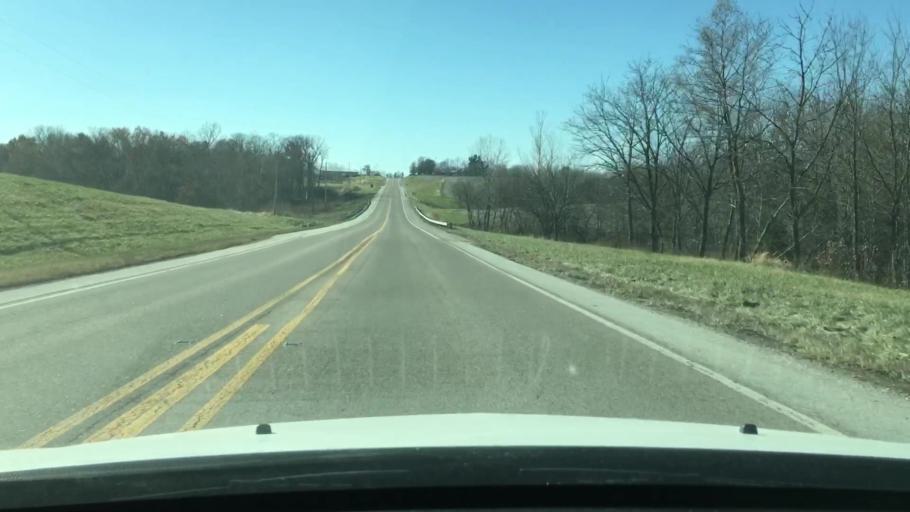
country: US
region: Illinois
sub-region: Pike County
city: Pittsfield
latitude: 39.6036
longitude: -90.8764
